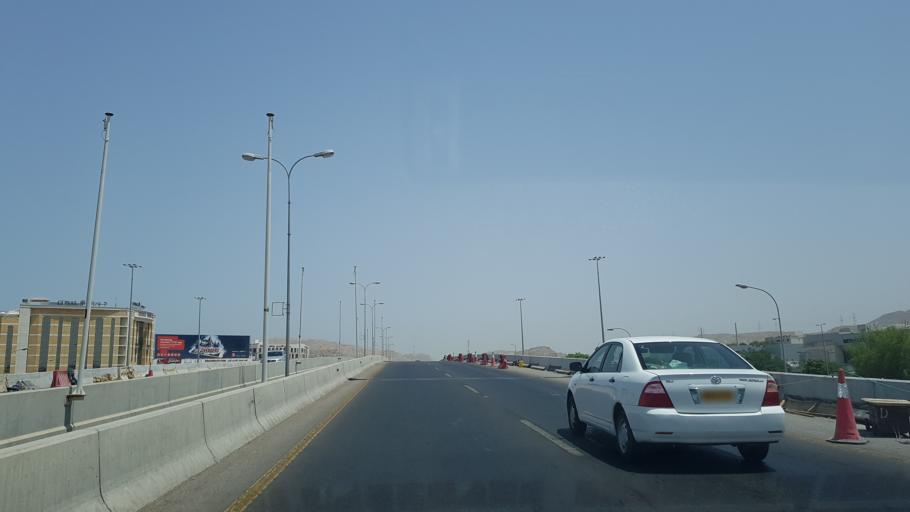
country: OM
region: Muhafazat Masqat
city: Muscat
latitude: 23.6122
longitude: 58.4911
